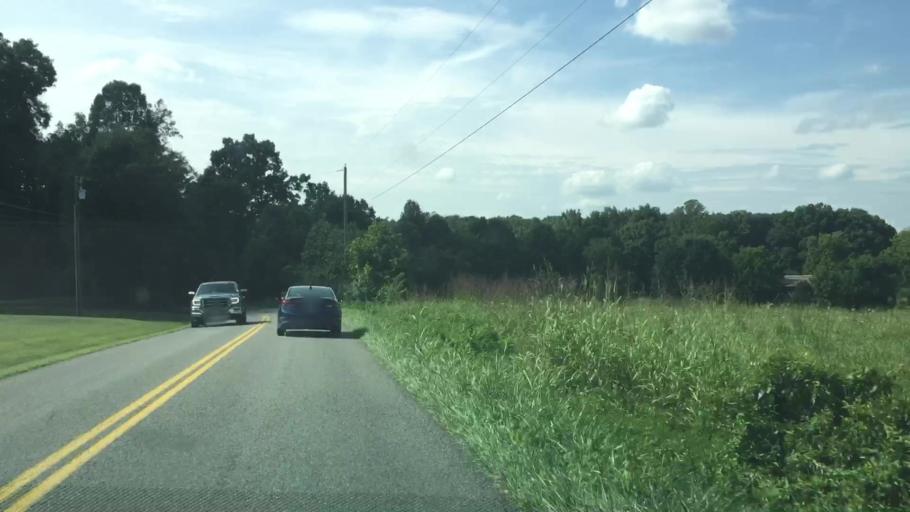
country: US
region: Tennessee
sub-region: Sullivan County
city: Fairmount
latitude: 36.5996
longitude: -82.0518
